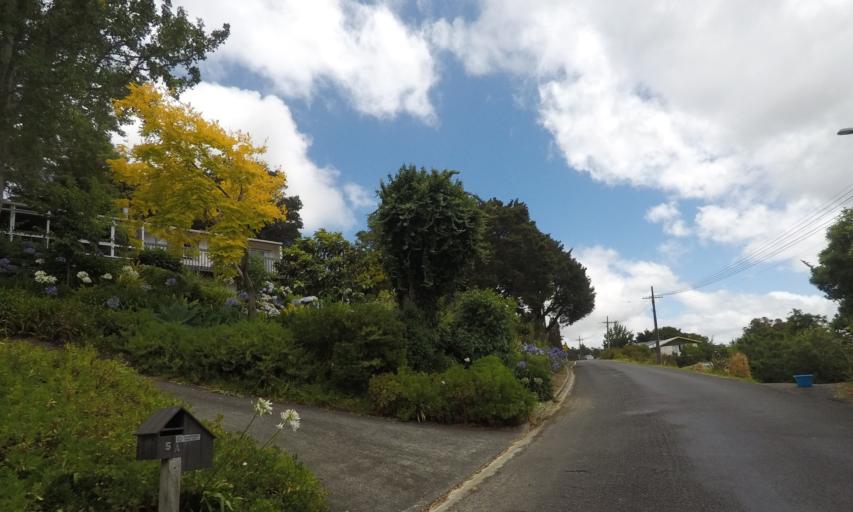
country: NZ
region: Northland
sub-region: Whangarei
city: Whangarei
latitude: -35.7427
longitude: 174.3613
